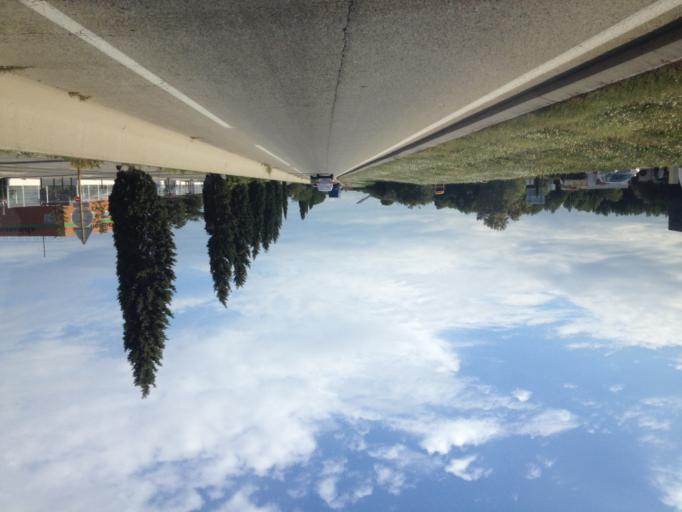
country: FR
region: Provence-Alpes-Cote d'Azur
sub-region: Departement du Vaucluse
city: Courthezon
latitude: 44.1097
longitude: 4.8501
